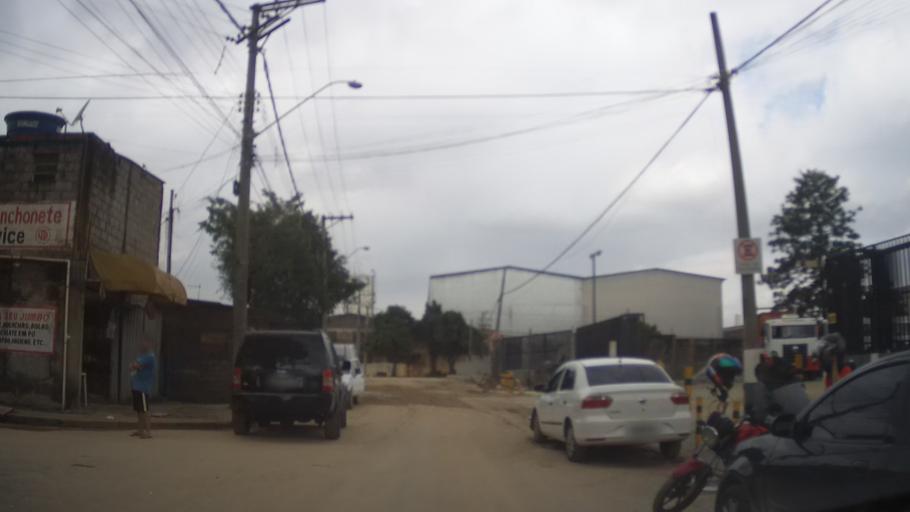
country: BR
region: Sao Paulo
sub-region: Guarulhos
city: Guarulhos
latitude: -23.4676
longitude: -46.4885
